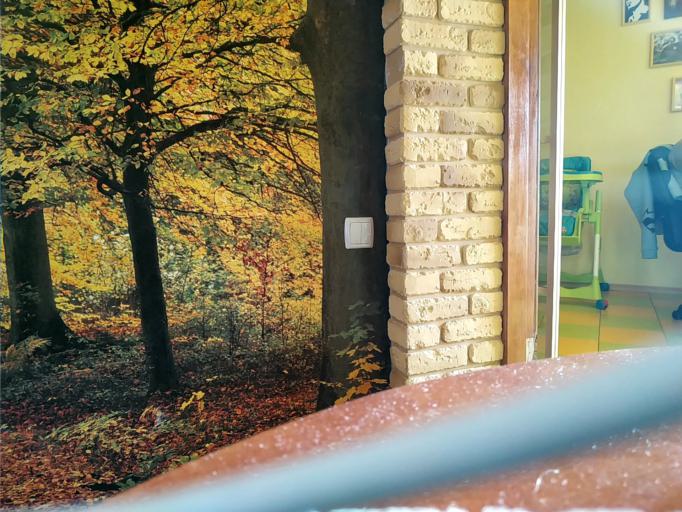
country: RU
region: Tverskaya
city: Rameshki
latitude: 57.3010
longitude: 35.9115
